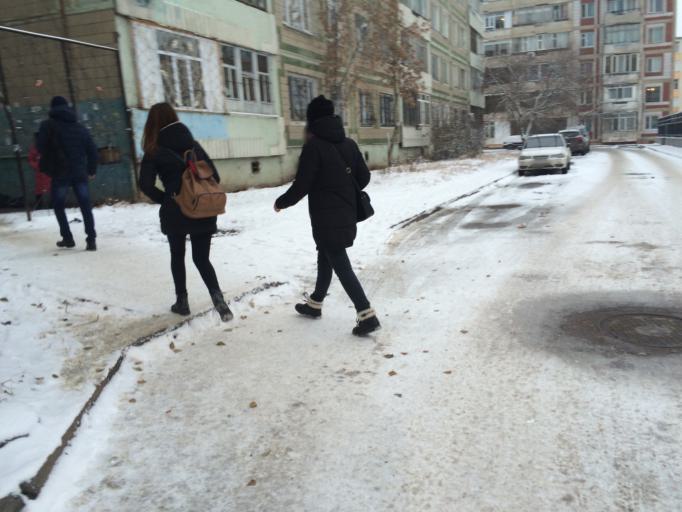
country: KZ
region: Astana Qalasy
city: Astana
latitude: 51.1792
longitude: 71.4337
